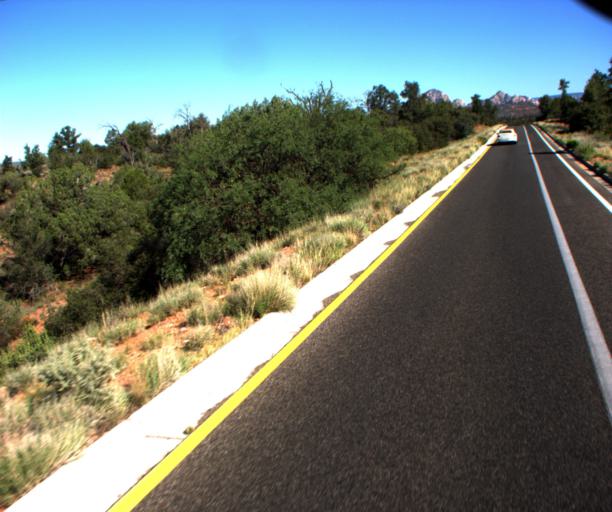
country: US
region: Arizona
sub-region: Yavapai County
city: Village of Oak Creek (Big Park)
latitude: 34.8132
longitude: -111.7657
